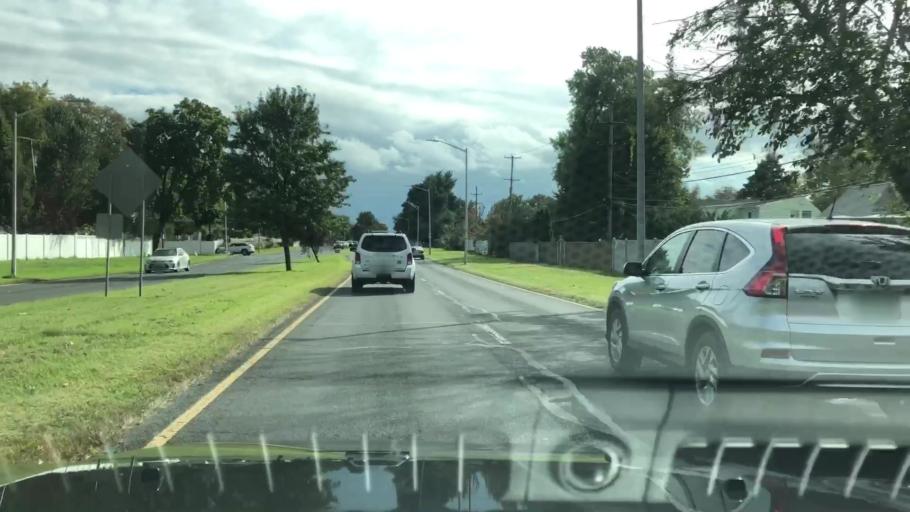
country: US
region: Pennsylvania
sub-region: Bucks County
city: Levittown
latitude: 40.1608
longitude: -74.8326
